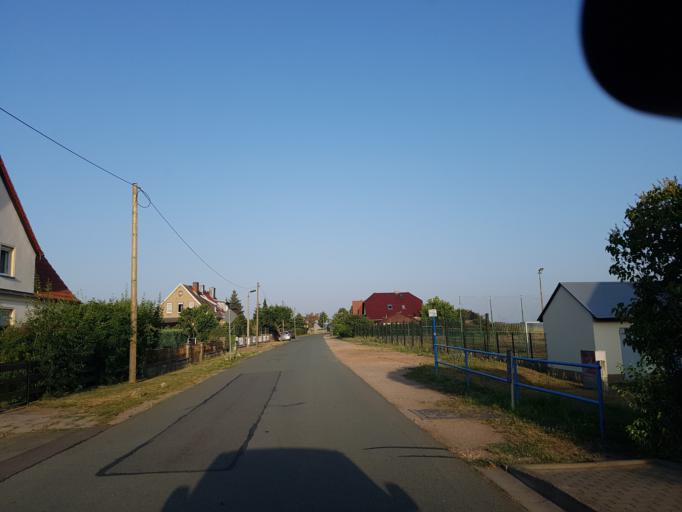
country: DE
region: Saxony
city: Strehla
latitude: 51.3540
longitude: 13.2173
